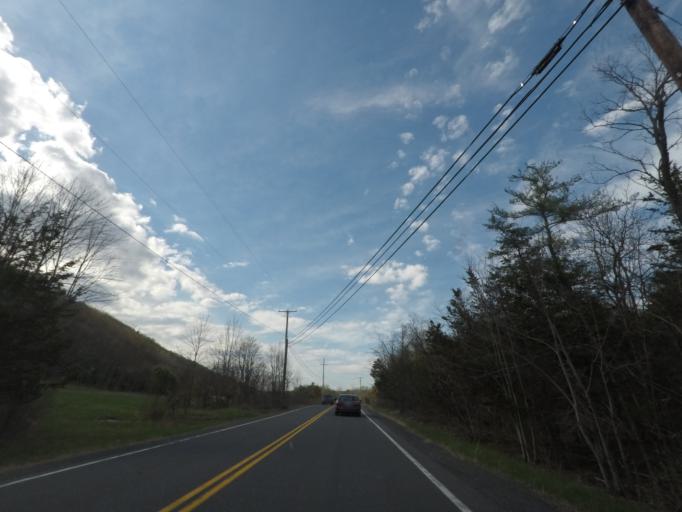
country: US
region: New York
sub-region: Albany County
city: Voorheesville
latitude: 42.5644
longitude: -73.9529
